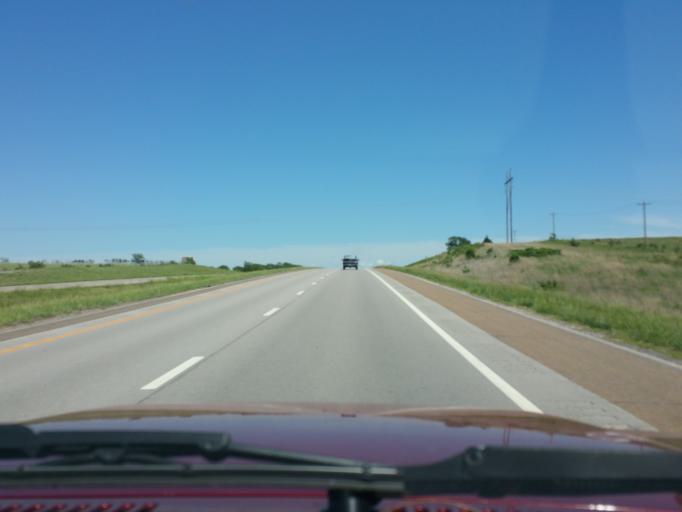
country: US
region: Kansas
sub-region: Pottawatomie County
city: Wamego
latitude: 39.2101
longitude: -96.3835
